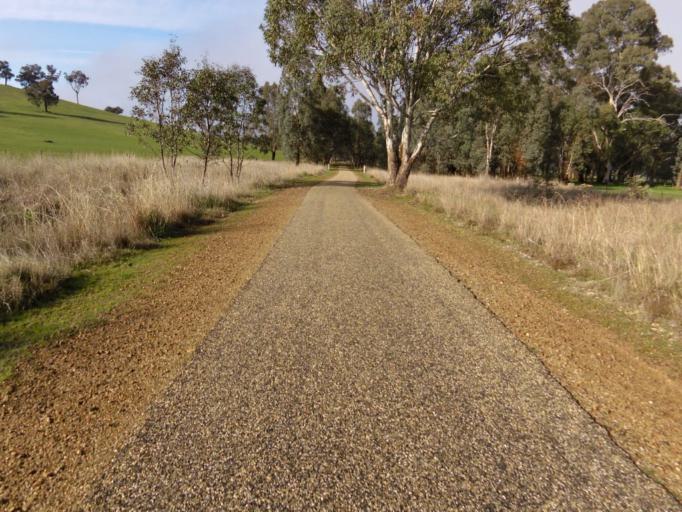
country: AU
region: Victoria
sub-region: Wangaratta
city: Wangaratta
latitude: -36.4456
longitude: 146.5512
